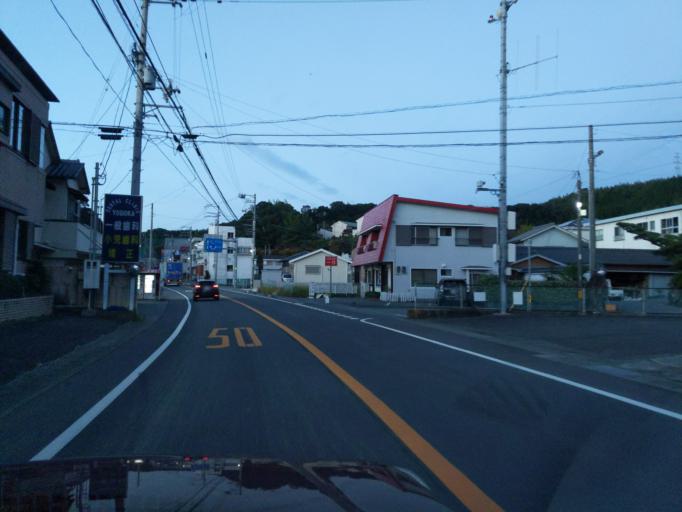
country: JP
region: Tokushima
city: Anan
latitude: 33.8721
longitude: 134.6357
